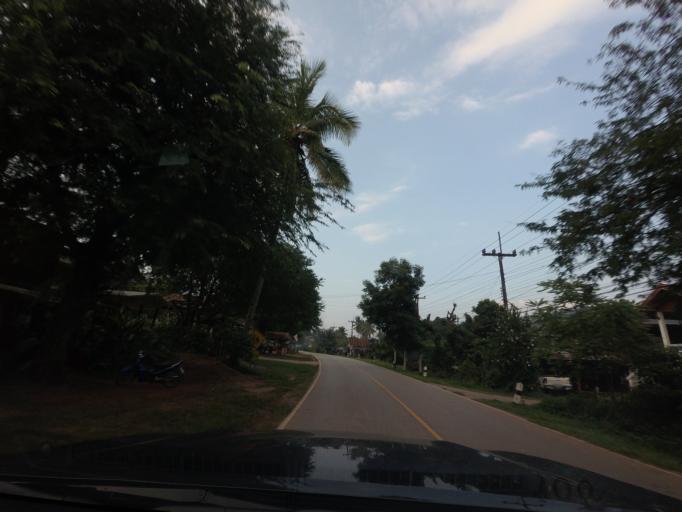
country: TH
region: Loei
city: Na Haeo
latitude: 17.4094
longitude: 101.0476
